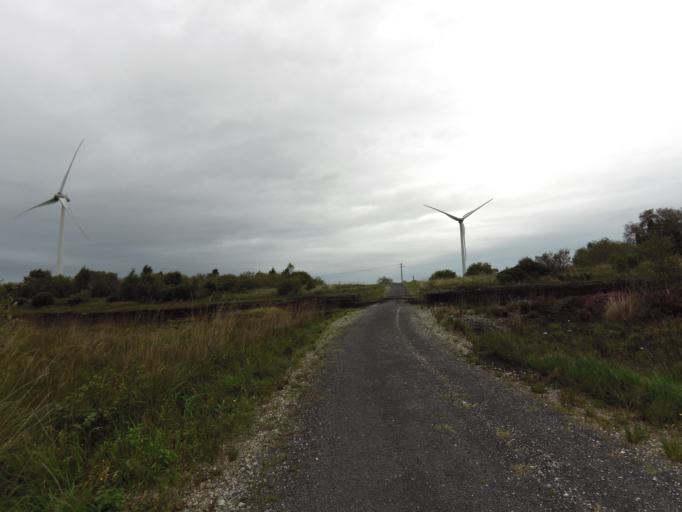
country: IE
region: Leinster
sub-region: Uibh Fhaili
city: Ferbane
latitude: 53.2303
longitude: -7.7675
